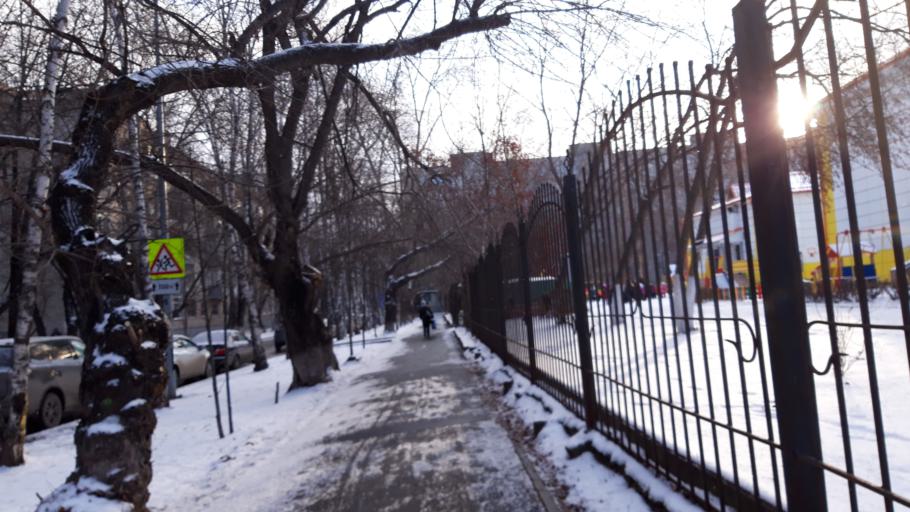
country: RU
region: Tjumen
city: Tyumen
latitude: 57.1513
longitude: 65.5501
